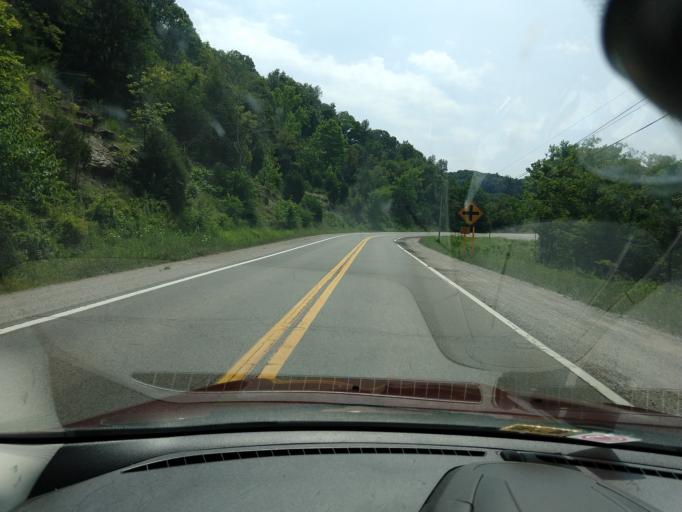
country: US
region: West Virginia
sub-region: Jackson County
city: Ravenswood
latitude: 38.8689
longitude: -81.8198
